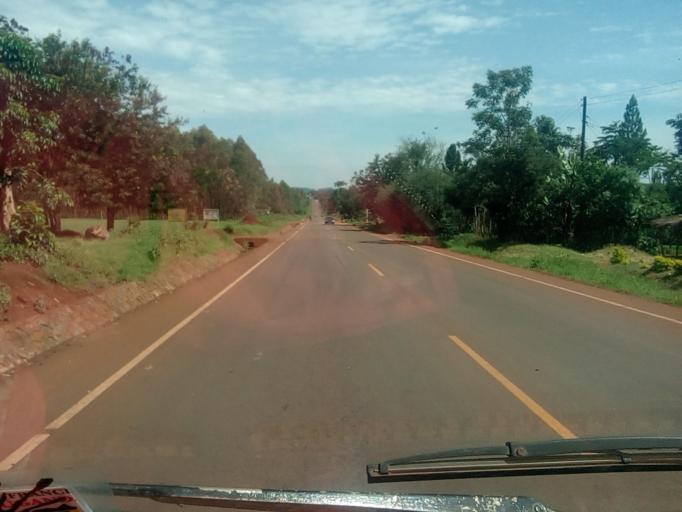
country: UG
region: Eastern Region
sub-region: Jinja District
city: Bugembe
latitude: 0.5648
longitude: 33.2445
